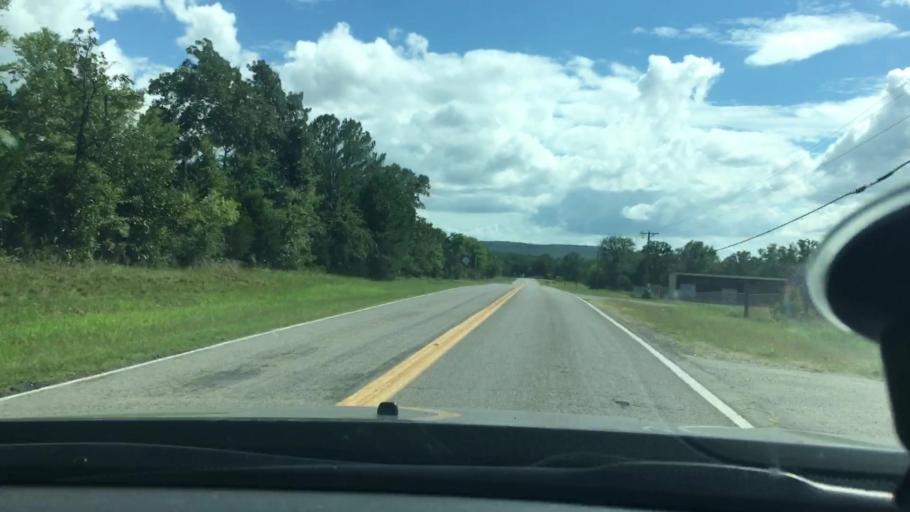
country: US
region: Oklahoma
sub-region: Cherokee County
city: Park Hill
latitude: 35.6990
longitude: -94.9144
